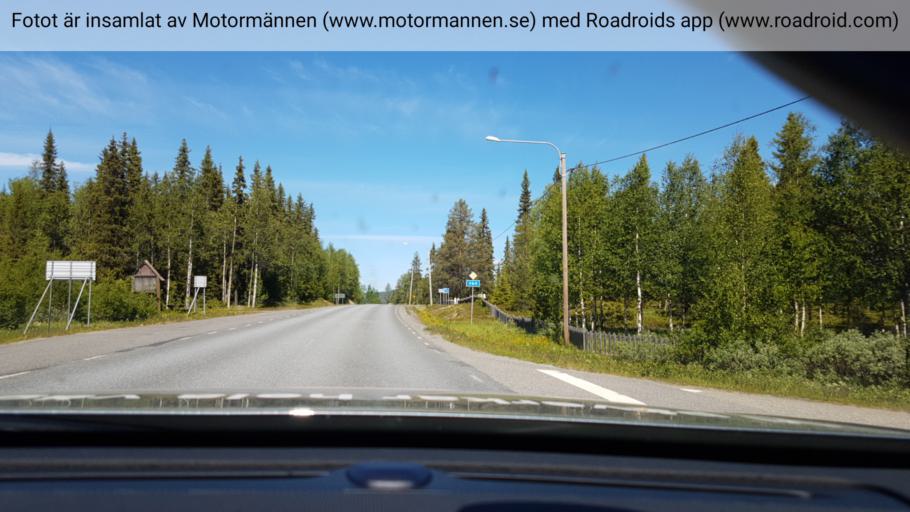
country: SE
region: Vaesterbotten
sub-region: Vilhelmina Kommun
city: Vilhelmina
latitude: 64.6436
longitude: 17.0763
